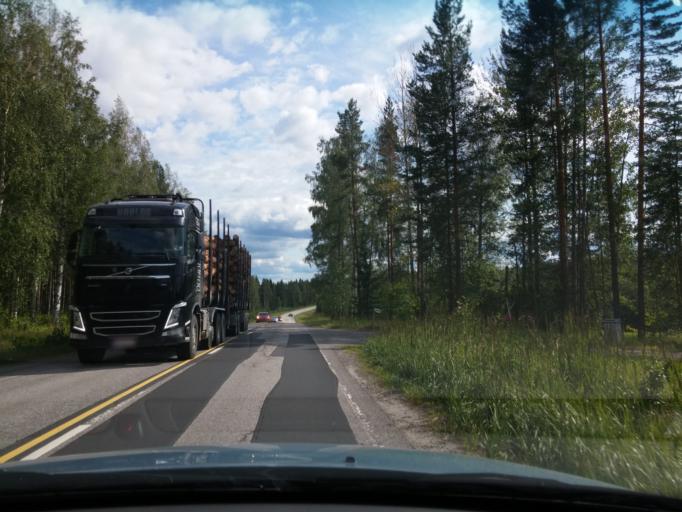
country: FI
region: Central Finland
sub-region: Keuruu
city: Keuruu
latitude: 62.3158
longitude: 24.7303
